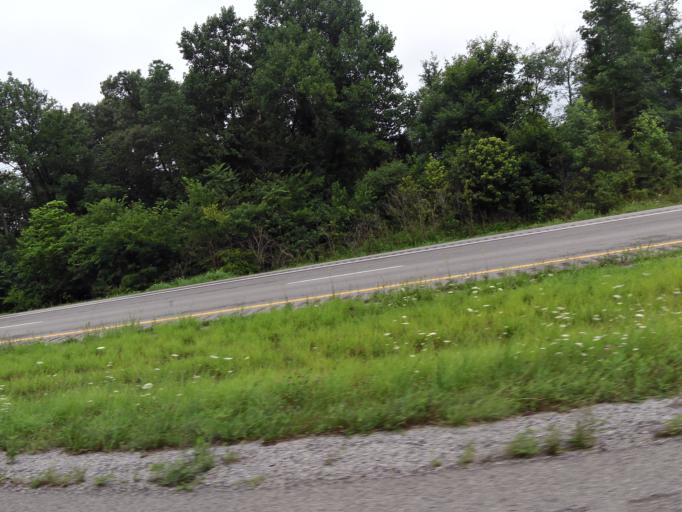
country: US
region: Kentucky
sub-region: Muhlenberg County
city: Central City
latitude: 37.3151
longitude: -87.0515
